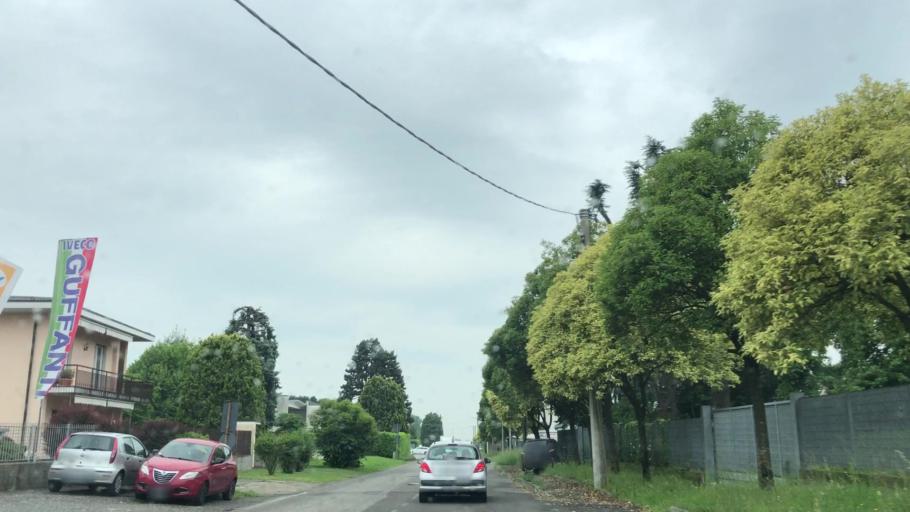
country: IT
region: Lombardy
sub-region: Provincia di Como
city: Fenegro
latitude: 45.6951
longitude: 8.9951
